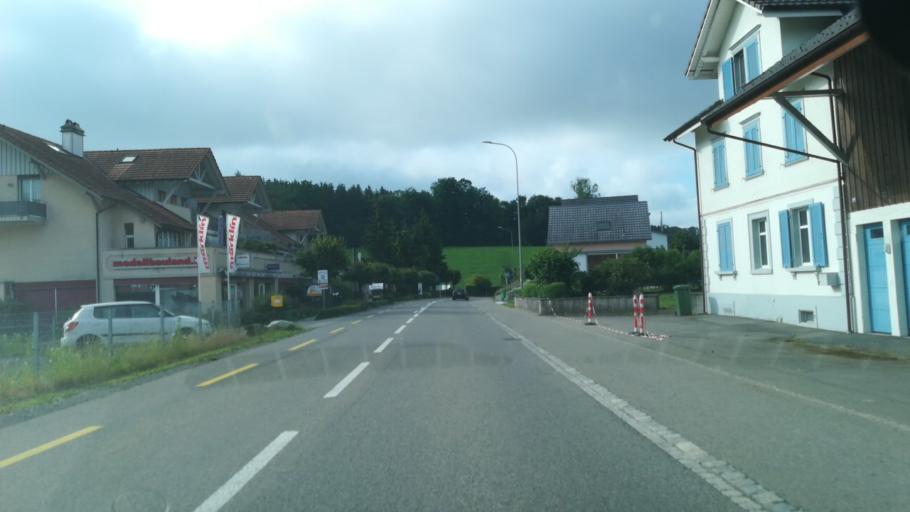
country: CH
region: Saint Gallen
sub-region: Wahlkreis St. Gallen
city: Waldkirch
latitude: 47.4846
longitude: 9.2568
